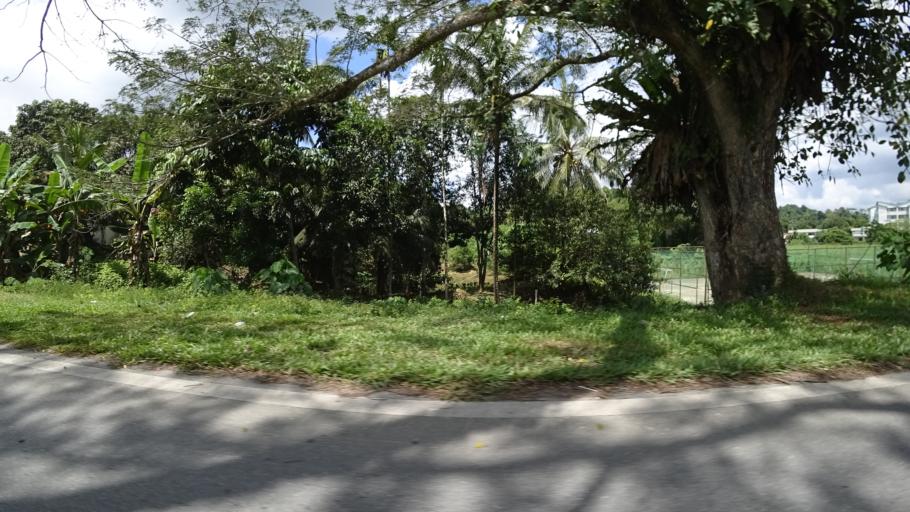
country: BN
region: Tutong
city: Tutong
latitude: 4.7278
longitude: 114.8024
